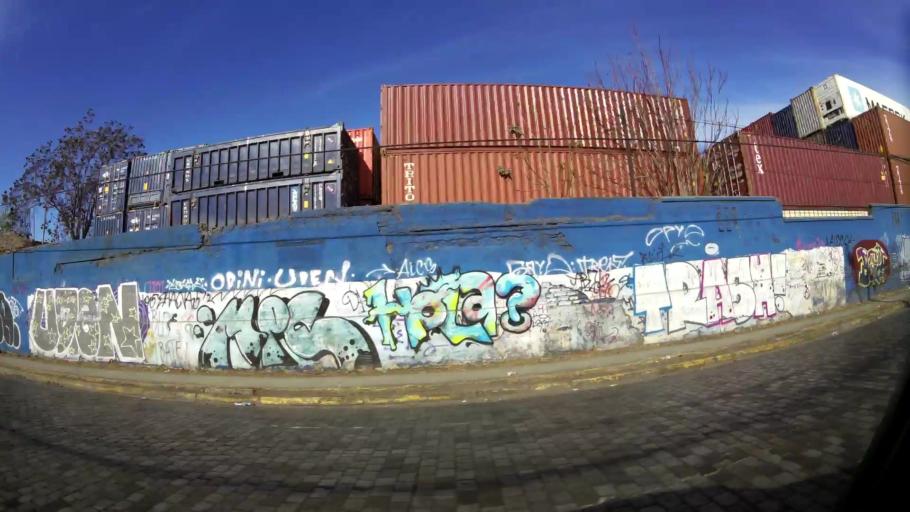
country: CL
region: Santiago Metropolitan
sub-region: Provincia de Santiago
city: Santiago
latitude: -33.4570
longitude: -70.6807
